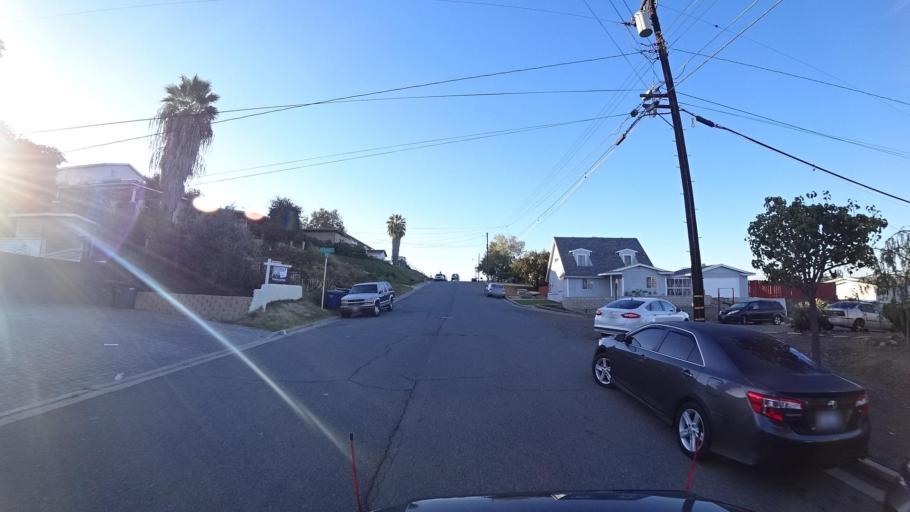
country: US
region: California
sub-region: San Diego County
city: La Presa
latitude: 32.7118
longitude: -117.0009
